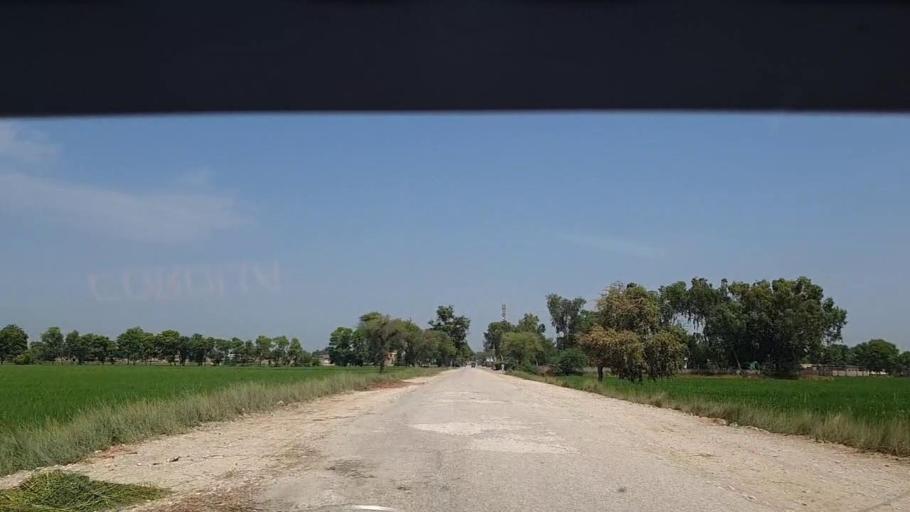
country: PK
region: Sindh
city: Rustam jo Goth
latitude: 28.0755
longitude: 68.7836
